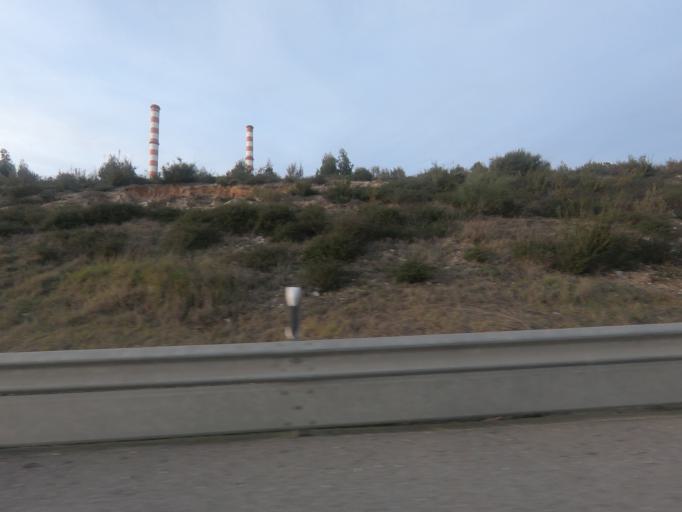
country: PT
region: Setubal
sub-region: Setubal
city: Setubal
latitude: 38.5068
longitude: -8.8412
